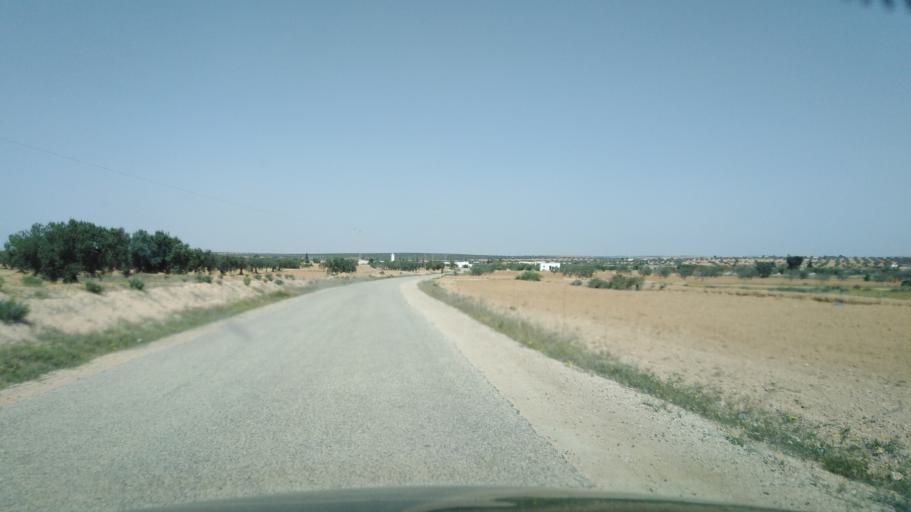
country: TN
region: Safaqis
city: Sfax
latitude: 34.6768
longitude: 10.4403
